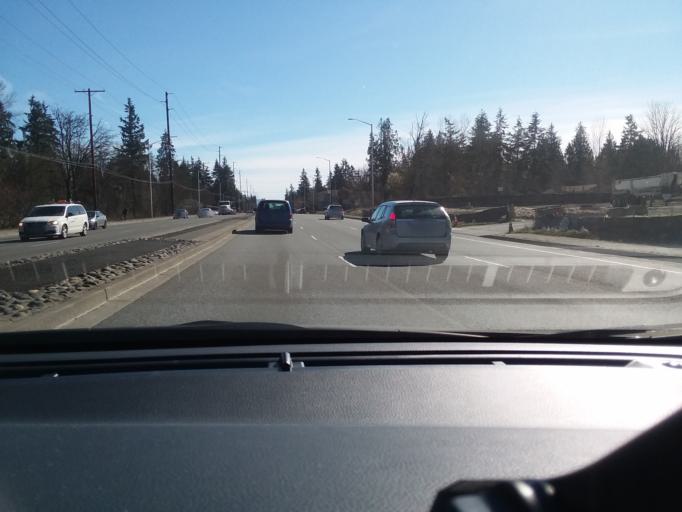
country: US
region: Washington
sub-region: Pierce County
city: Frederickson
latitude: 47.1206
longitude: -122.3577
